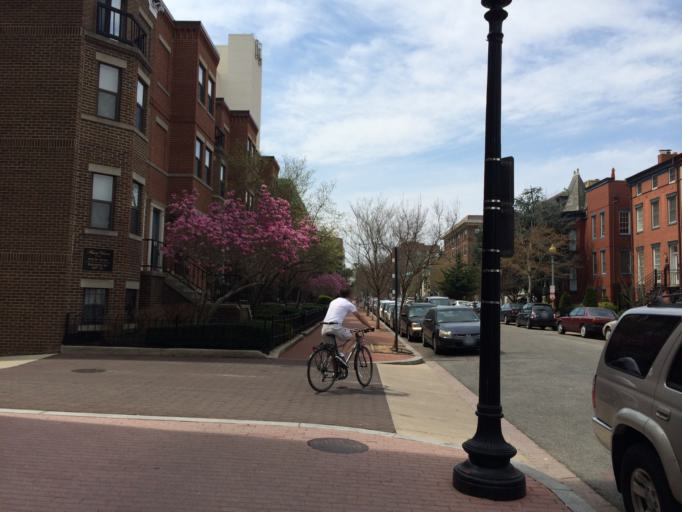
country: US
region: Washington, D.C.
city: Washington, D.C.
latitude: 38.9057
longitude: -77.0249
